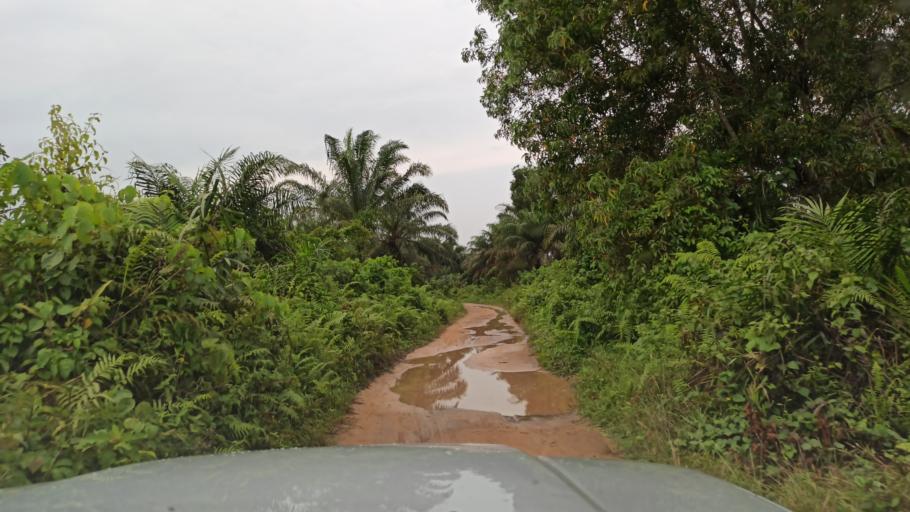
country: BJ
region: Queme
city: Porto-Novo
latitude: 6.4616
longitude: 2.6755
